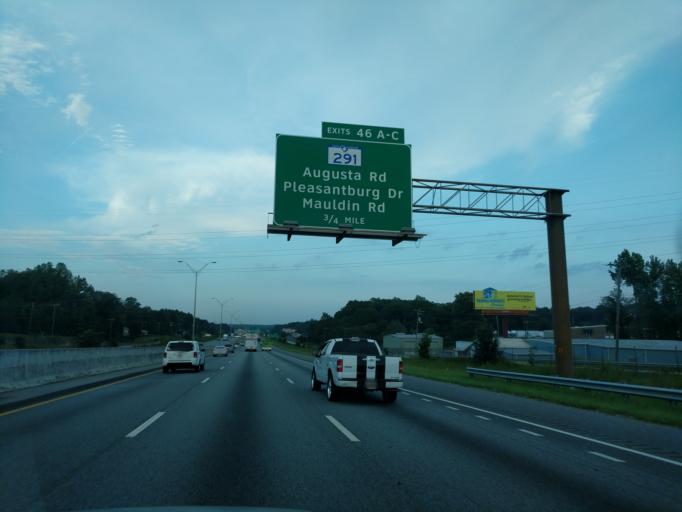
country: US
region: South Carolina
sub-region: Greenville County
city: Gantt
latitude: 34.7931
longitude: -82.3997
